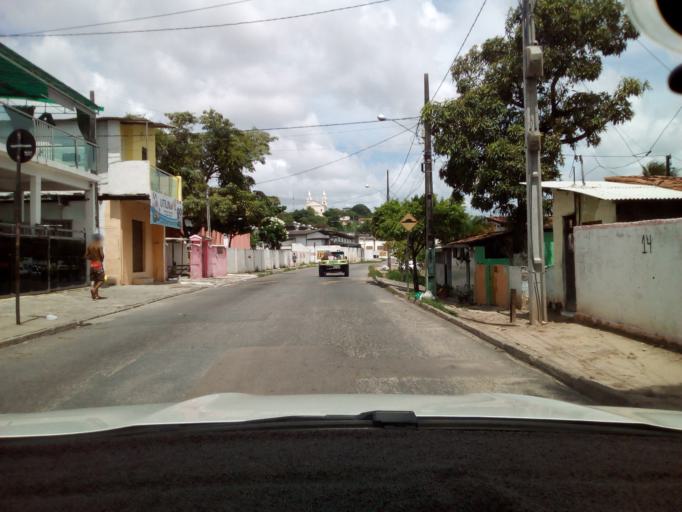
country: BR
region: Paraiba
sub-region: Joao Pessoa
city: Joao Pessoa
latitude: -7.1094
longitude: -34.8841
